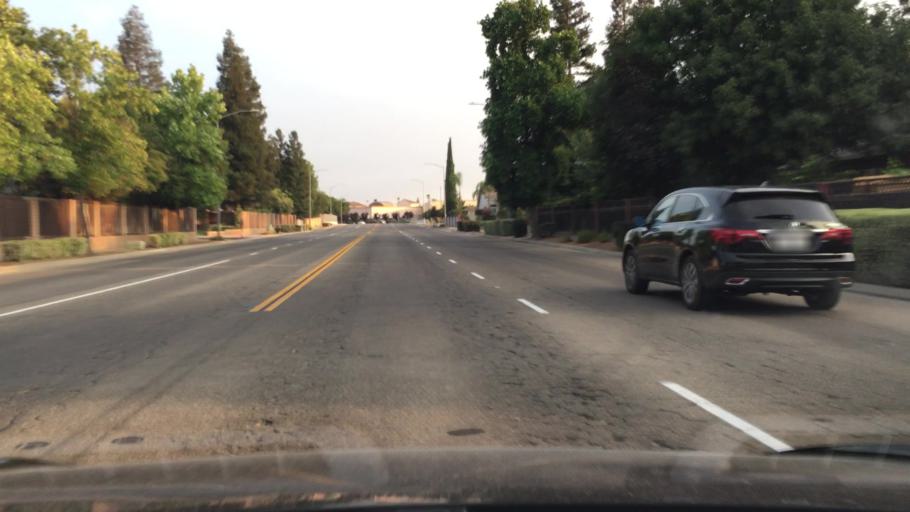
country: US
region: California
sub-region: Fresno County
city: Clovis
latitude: 36.8432
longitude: -119.6930
